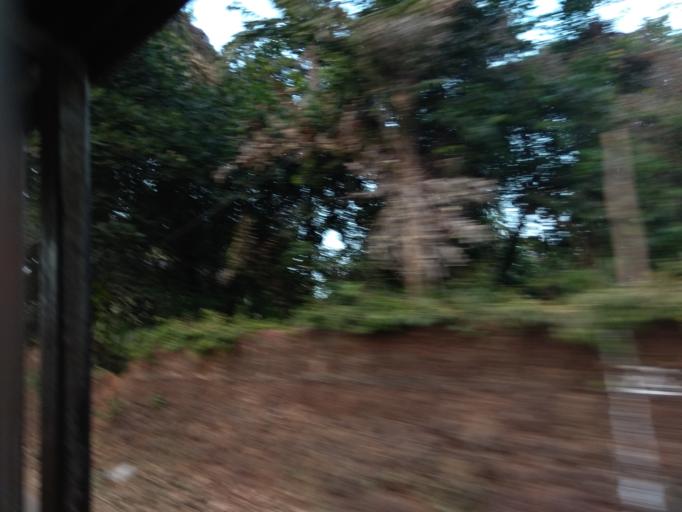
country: IN
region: Karnataka
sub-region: Dakshina Kannada
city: Mangalore
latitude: 12.9266
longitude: 74.8676
